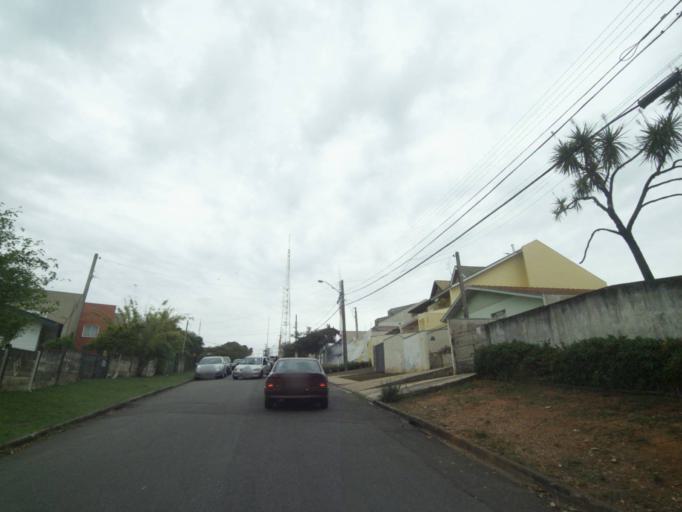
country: BR
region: Parana
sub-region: Curitiba
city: Curitiba
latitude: -25.3956
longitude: -49.2894
